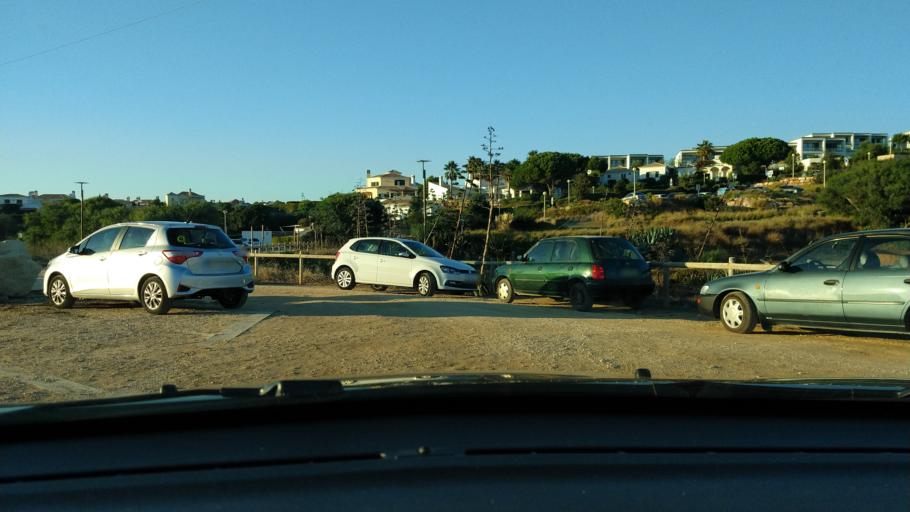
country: PT
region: Faro
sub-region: Vila do Bispo
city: Sagres
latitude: 37.0206
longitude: -8.9256
